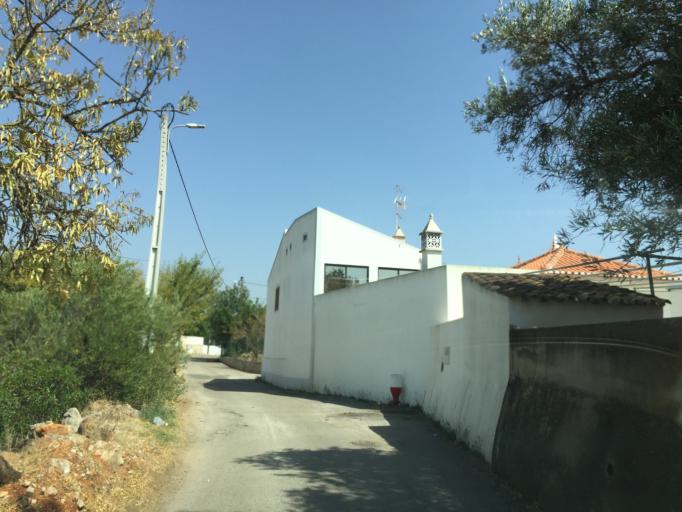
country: PT
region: Faro
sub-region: Loule
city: Boliqueime
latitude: 37.1200
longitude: -8.1916
